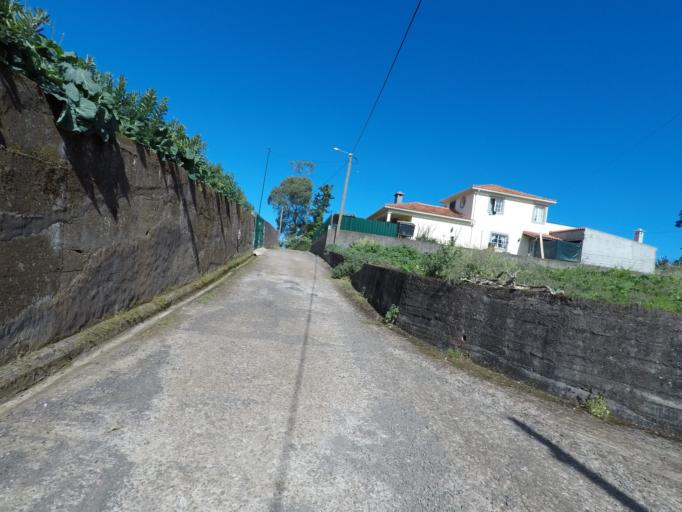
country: PT
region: Madeira
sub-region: Santana
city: Santana
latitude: 32.8220
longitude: -16.9401
